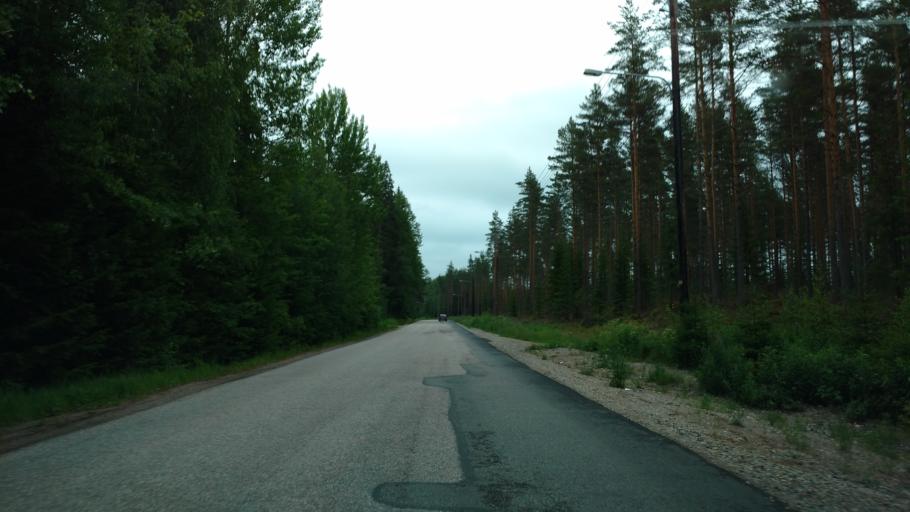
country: FI
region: Varsinais-Suomi
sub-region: Salo
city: Kiikala
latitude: 60.4293
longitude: 23.5925
